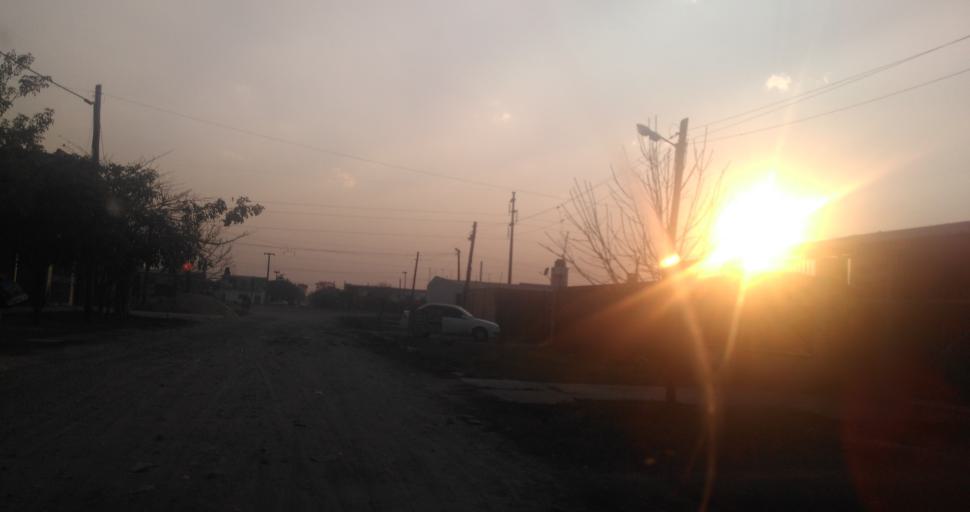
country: AR
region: Chaco
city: Resistencia
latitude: -27.4764
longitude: -59.0041
